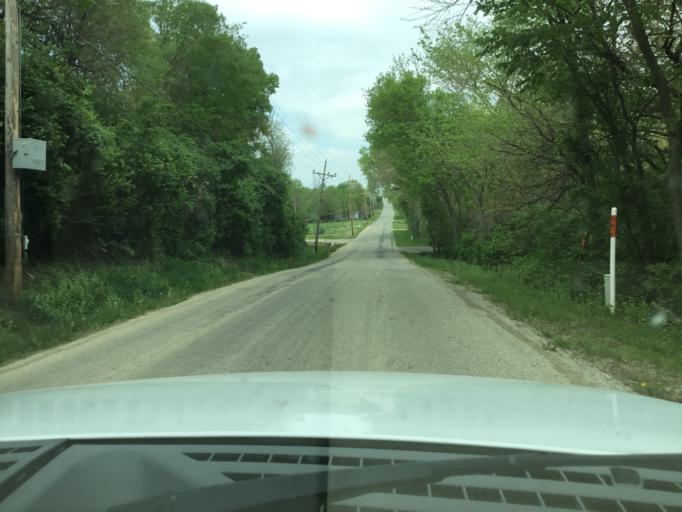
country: US
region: Kansas
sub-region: Shawnee County
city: Topeka
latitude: 39.0183
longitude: -95.5860
